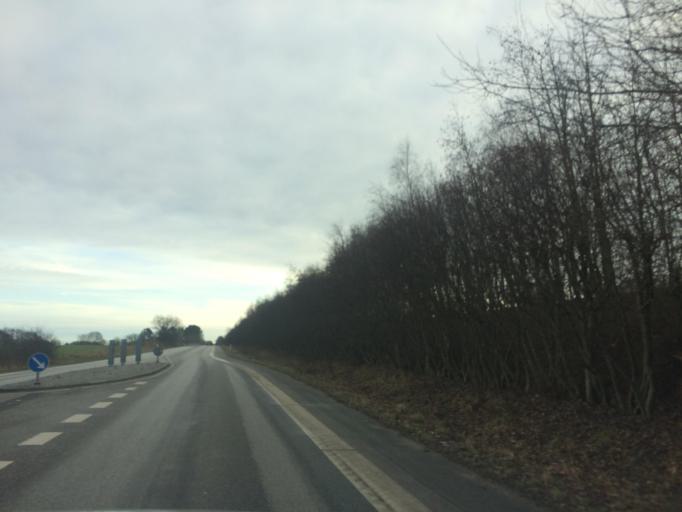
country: DK
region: Capital Region
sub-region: Fredensborg Kommune
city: Fredensborg
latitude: 55.9630
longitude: 12.4083
